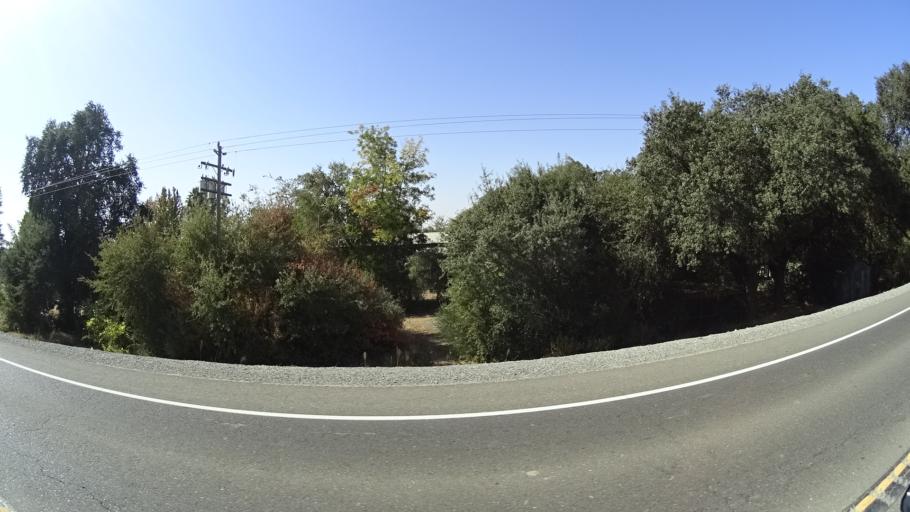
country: US
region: California
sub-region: Yolo County
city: West Sacramento
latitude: 38.6220
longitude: -121.5634
